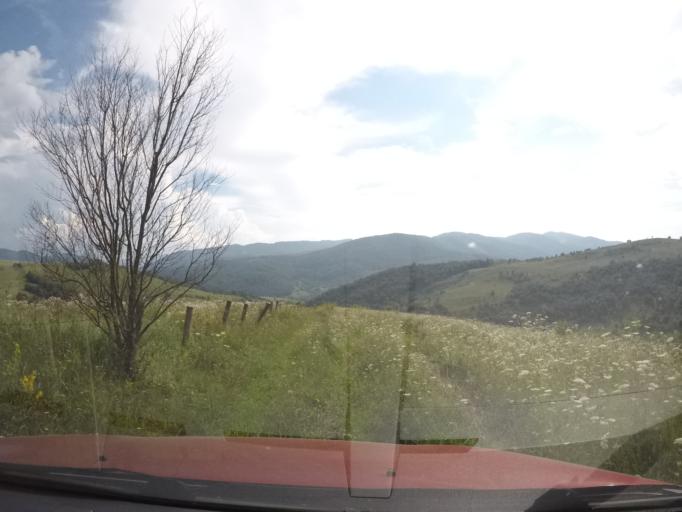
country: UA
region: Zakarpattia
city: Velykyi Bereznyi
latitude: 49.0267
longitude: 22.6394
